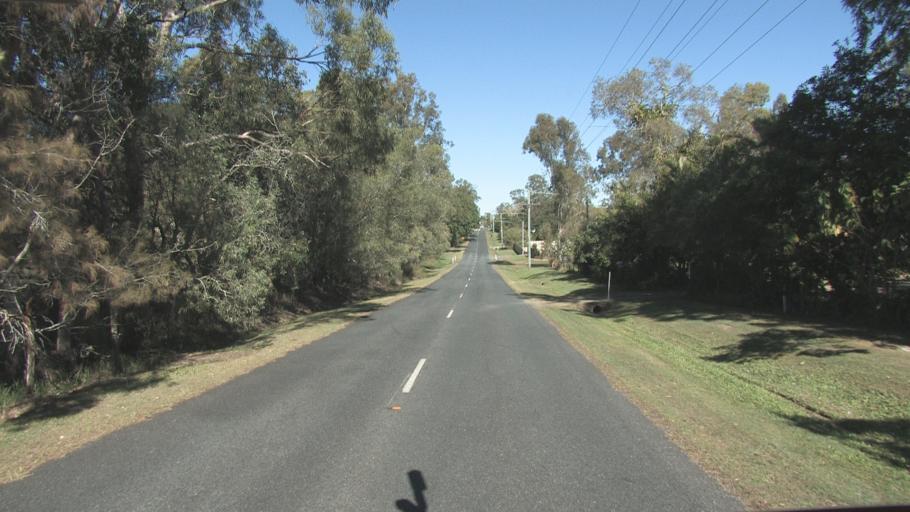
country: AU
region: Queensland
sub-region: Logan
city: Park Ridge South
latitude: -27.7159
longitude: 153.0578
